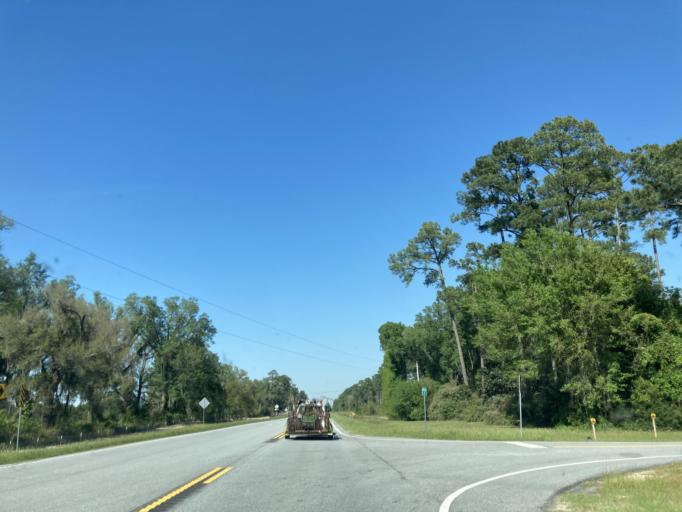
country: US
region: Georgia
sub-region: Dougherty County
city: Putney
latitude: 31.4466
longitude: -84.2649
